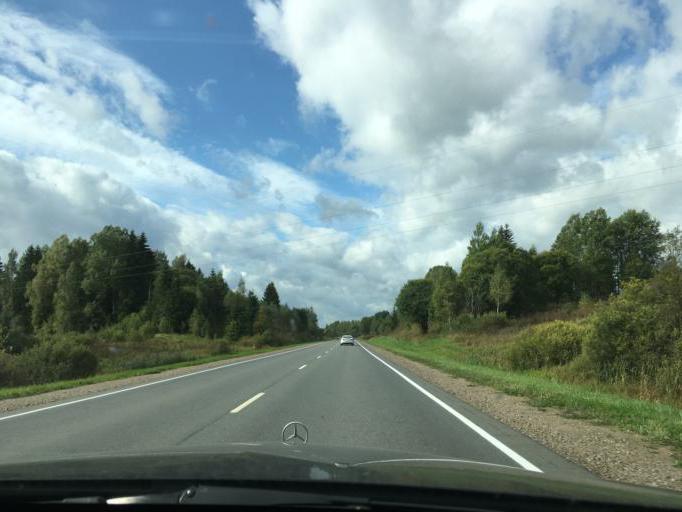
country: RU
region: Tverskaya
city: Toropets
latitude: 56.3391
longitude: 31.3225
